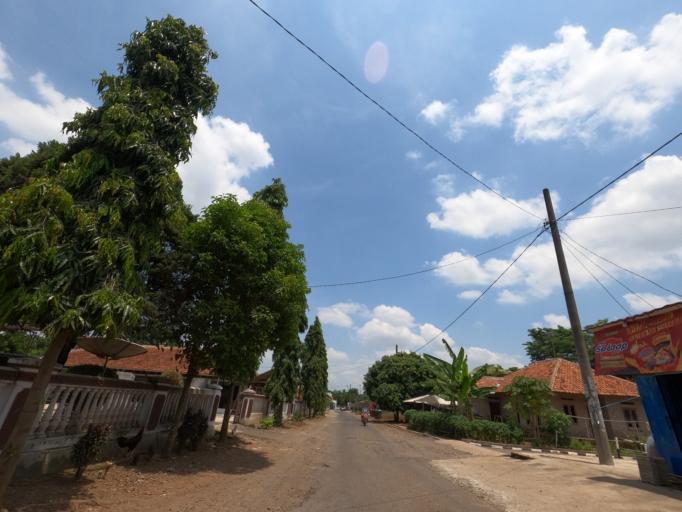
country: ID
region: West Java
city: Pamanukan
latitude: -6.5195
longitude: 107.7772
